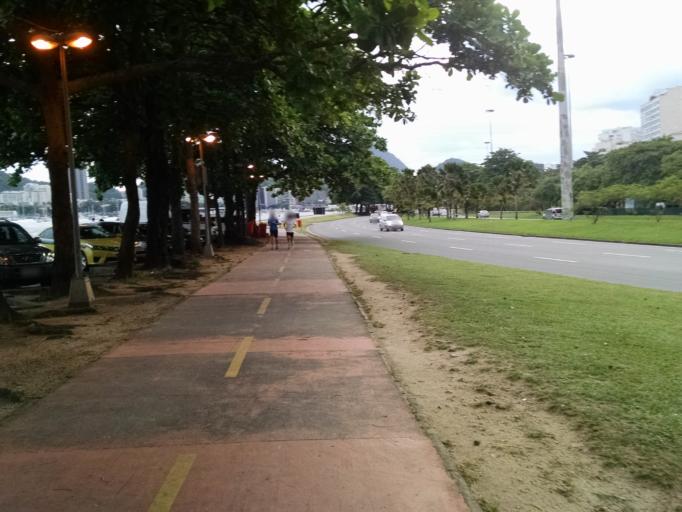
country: BR
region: Rio de Janeiro
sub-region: Rio De Janeiro
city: Rio de Janeiro
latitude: -22.9404
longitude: -43.1701
